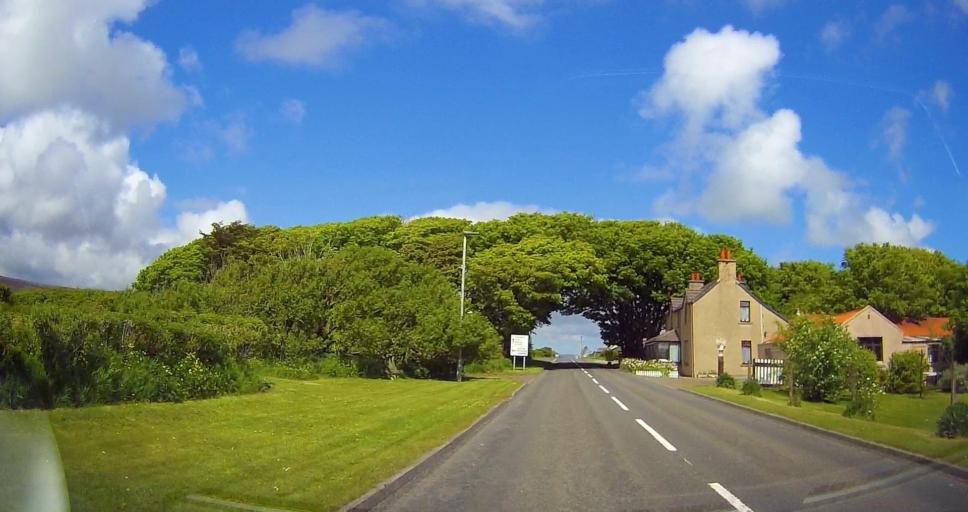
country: GB
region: Scotland
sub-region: Orkney Islands
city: Orkney
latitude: 59.0457
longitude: -3.0838
